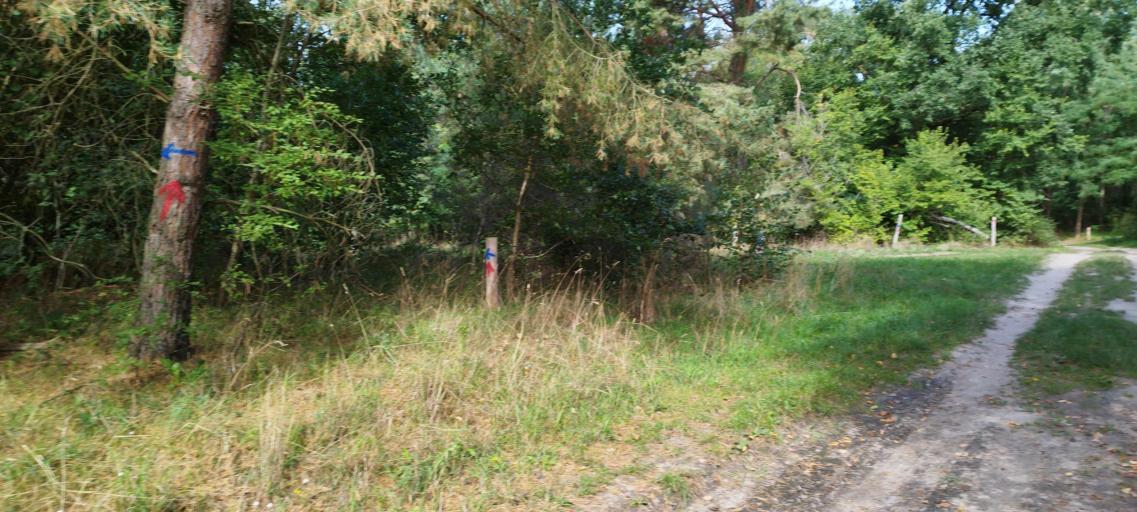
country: DE
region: Brandenburg
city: Dallgow-Doeberitz
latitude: 52.5313
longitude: 13.0486
